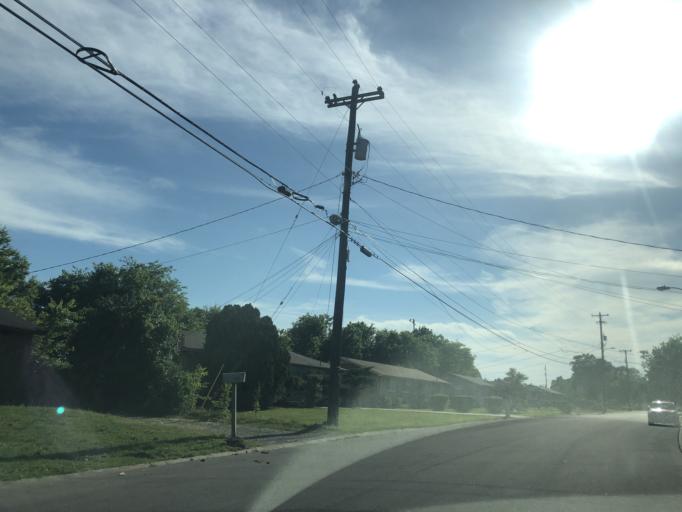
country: US
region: Tennessee
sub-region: Davidson County
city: Nashville
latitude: 36.2116
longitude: -86.8356
